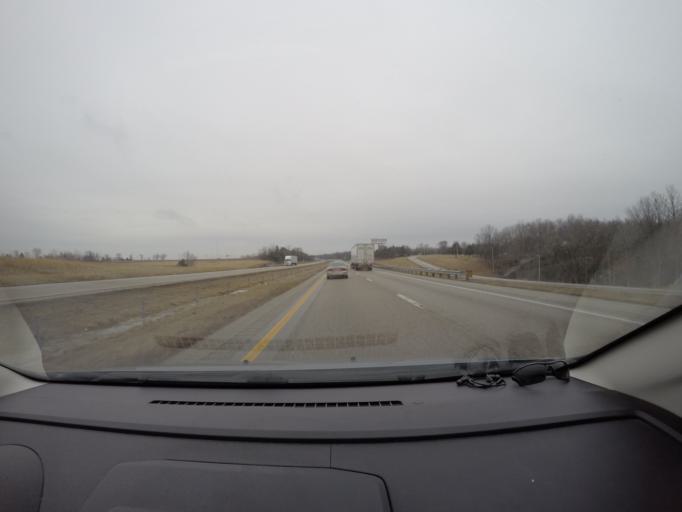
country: US
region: Missouri
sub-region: Montgomery County
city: Montgomery City
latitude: 38.8692
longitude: -91.3614
